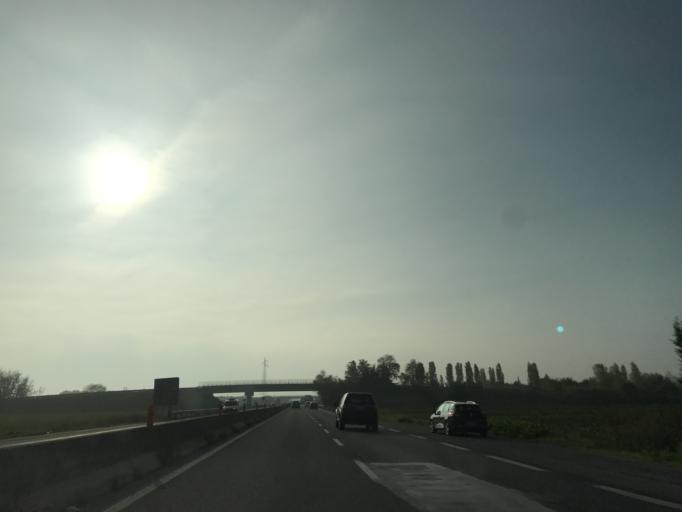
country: IT
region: Emilia-Romagna
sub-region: Provincia di Rimini
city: Bellaria-Igea Marina
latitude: 44.1381
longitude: 12.4605
